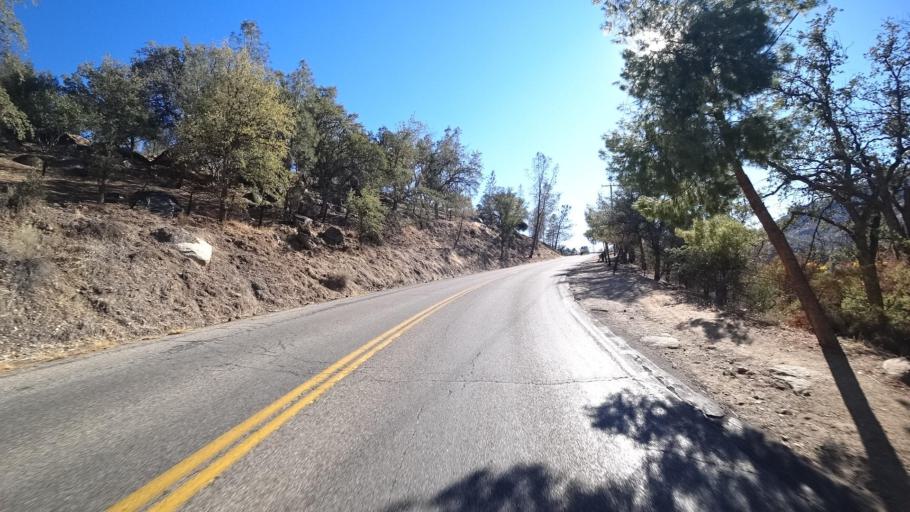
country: US
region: California
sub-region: Kern County
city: Kernville
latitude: 35.7608
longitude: -118.4203
